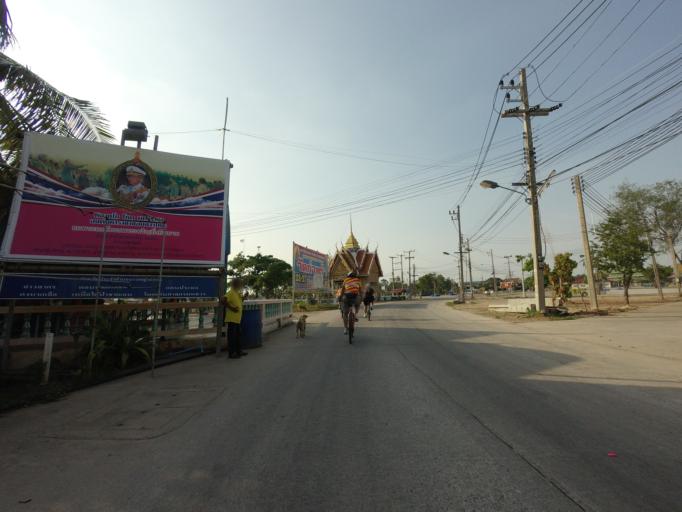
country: TH
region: Samut Sakhon
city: Samut Sakhon
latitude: 13.5180
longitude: 100.2762
